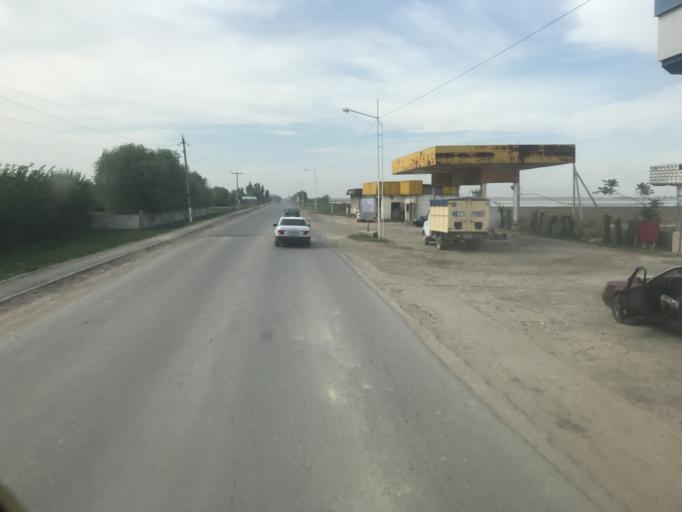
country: KZ
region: Ongtustik Qazaqstan
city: Asykata
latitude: 41.0027
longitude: 68.2139
